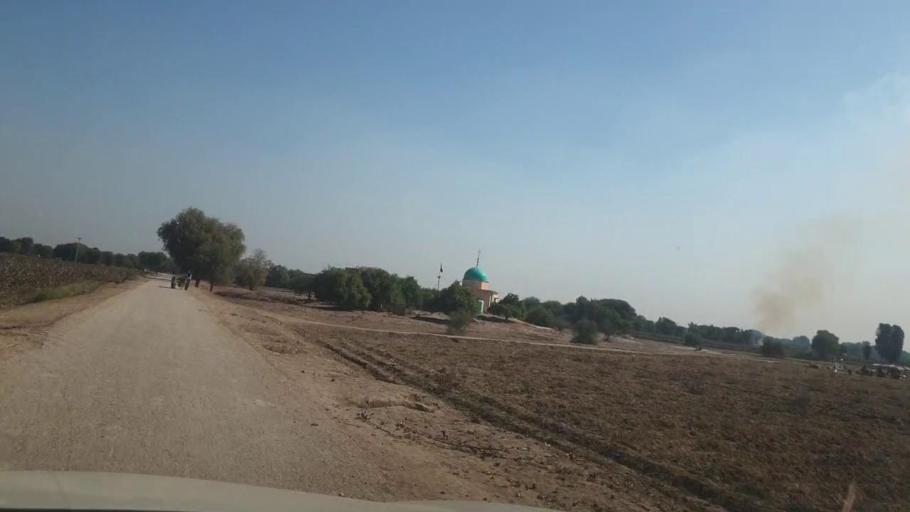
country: PK
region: Sindh
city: Bhan
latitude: 26.5794
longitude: 67.7043
